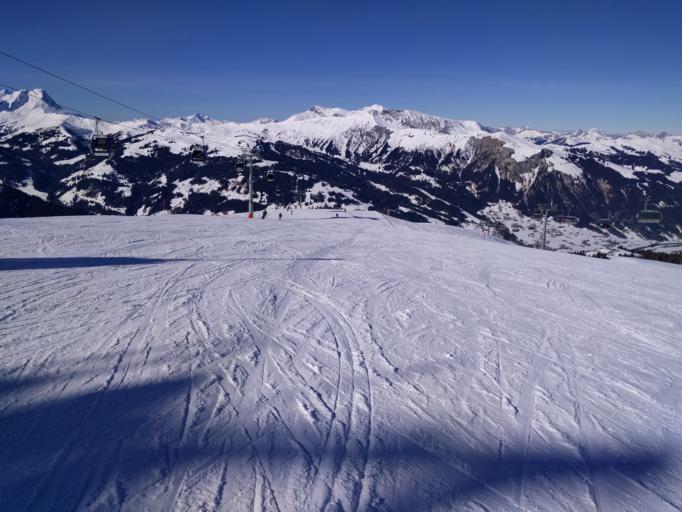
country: CH
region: Bern
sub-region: Obersimmental-Saanen District
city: Lenk
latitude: 46.4447
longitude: 7.4947
